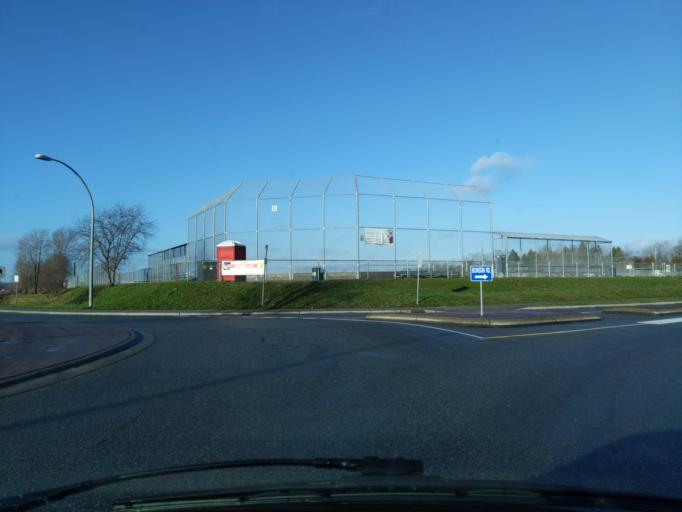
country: CA
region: British Columbia
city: Pitt Meadows
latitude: 49.2085
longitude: -122.6782
